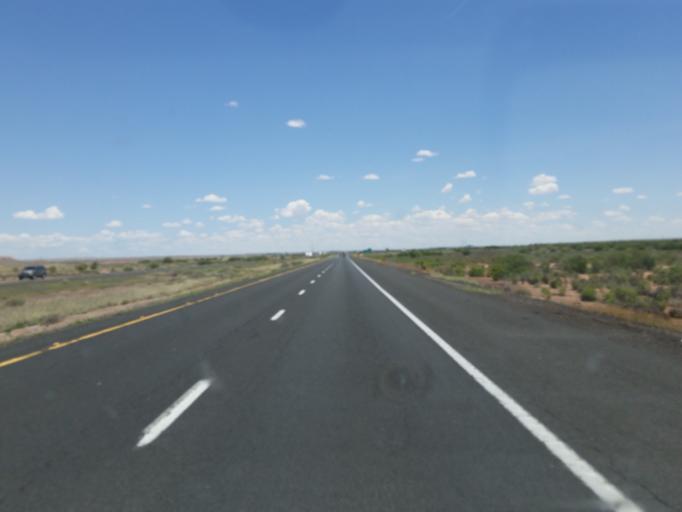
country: US
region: Arizona
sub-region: Navajo County
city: Joseph City
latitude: 34.9707
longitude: -110.4619
